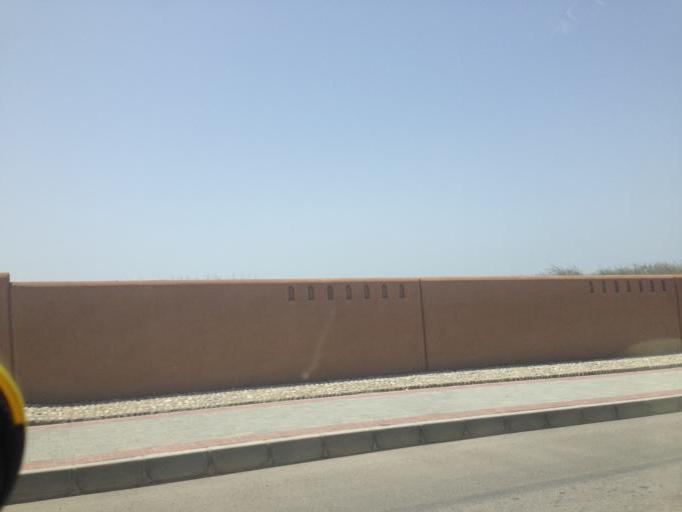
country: OM
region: Muhafazat Masqat
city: As Sib al Jadidah
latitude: 23.6923
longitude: 58.1064
